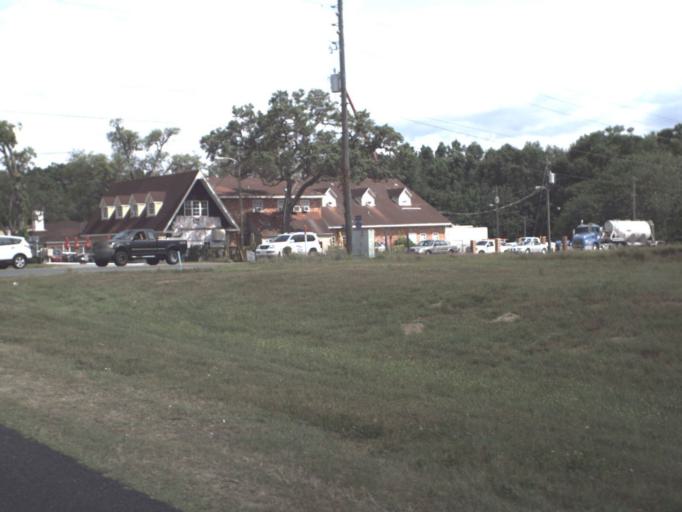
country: US
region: Florida
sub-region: Marion County
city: Ocala
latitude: 29.2283
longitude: -82.2357
